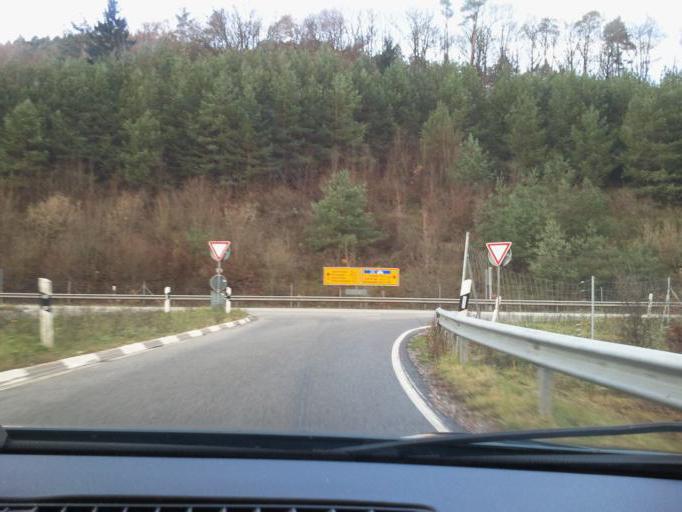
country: DE
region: Rheinland-Pfalz
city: Rinnthal
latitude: 49.2244
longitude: 7.9125
